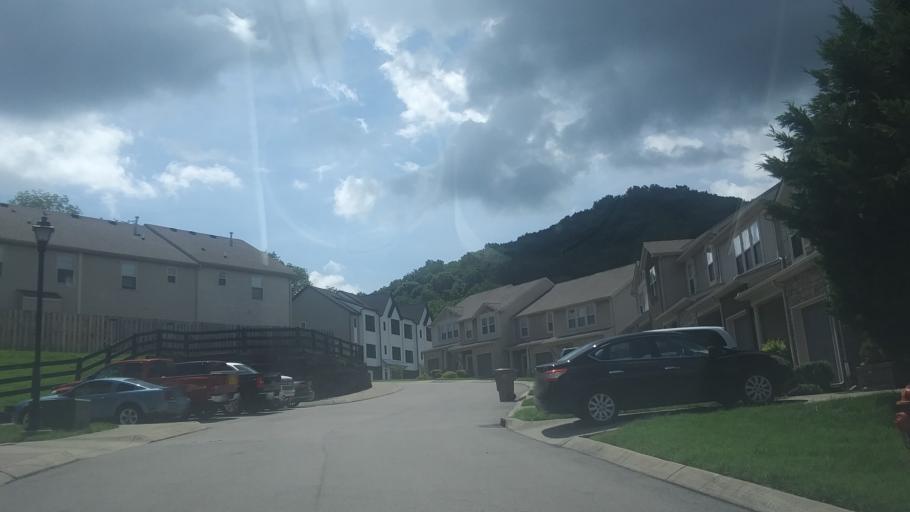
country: US
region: Tennessee
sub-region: Davidson County
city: Belle Meade
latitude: 36.1117
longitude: -86.9187
